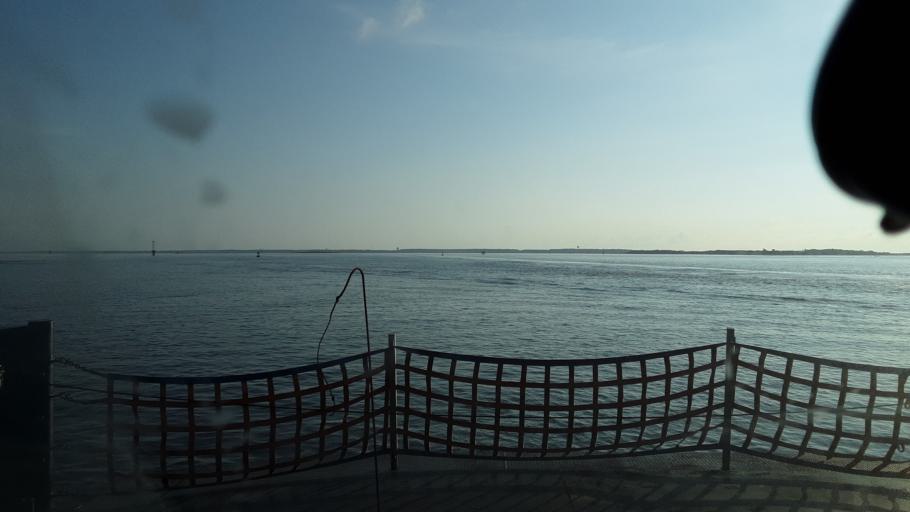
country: US
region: North Carolina
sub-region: New Hanover County
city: Kure Beach
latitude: 33.9549
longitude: -77.9592
